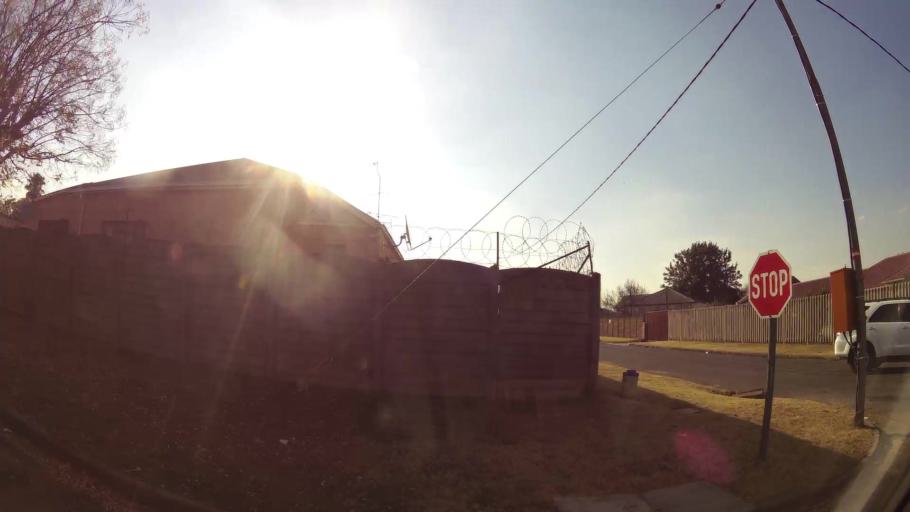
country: ZA
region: Gauteng
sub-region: Ekurhuleni Metropolitan Municipality
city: Brakpan
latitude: -26.2316
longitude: 28.3595
